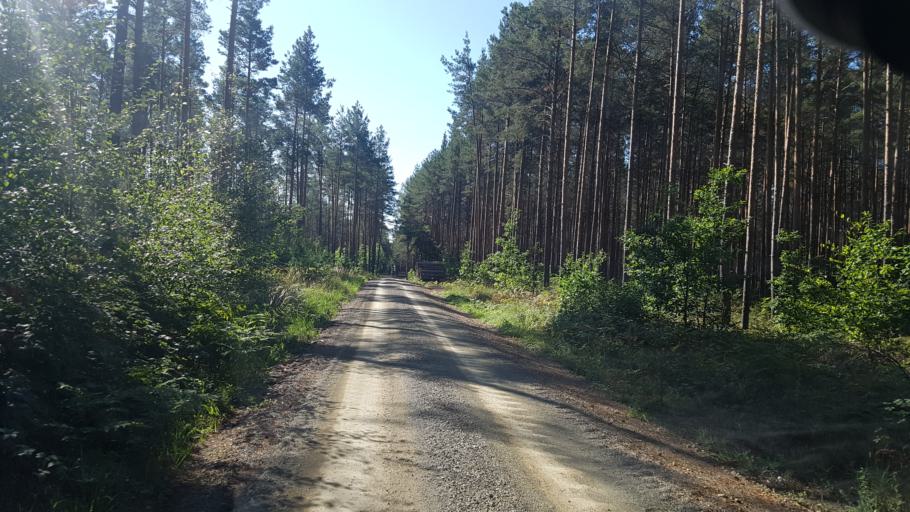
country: DE
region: Brandenburg
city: Ruckersdorf
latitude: 51.5375
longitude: 13.5820
